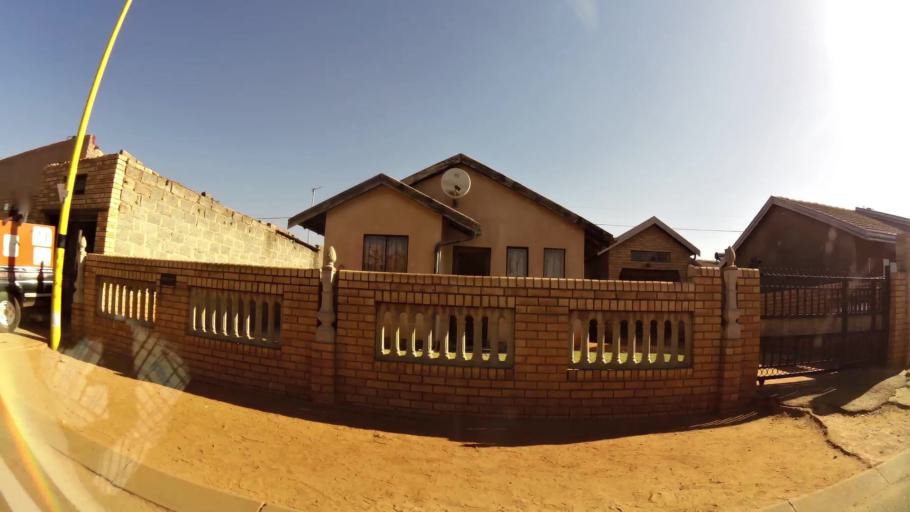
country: ZA
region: Gauteng
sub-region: Ekurhuleni Metropolitan Municipality
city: Tembisa
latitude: -26.0229
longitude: 28.2315
